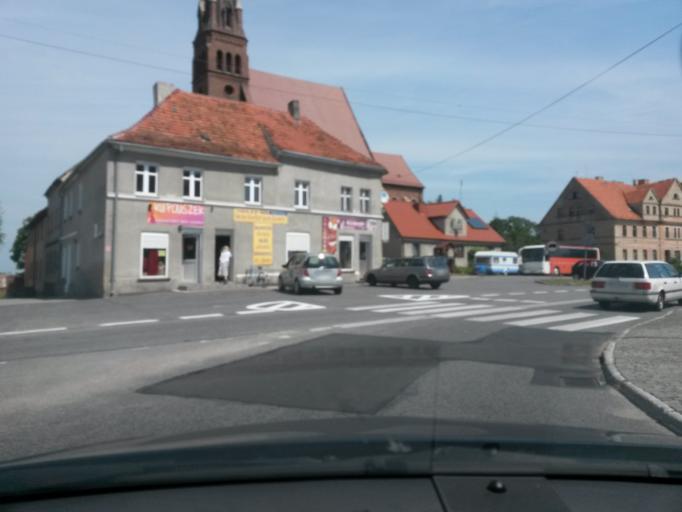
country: PL
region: Lower Silesian Voivodeship
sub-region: Powiat wolowski
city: Winsko
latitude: 51.4707
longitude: 16.6150
